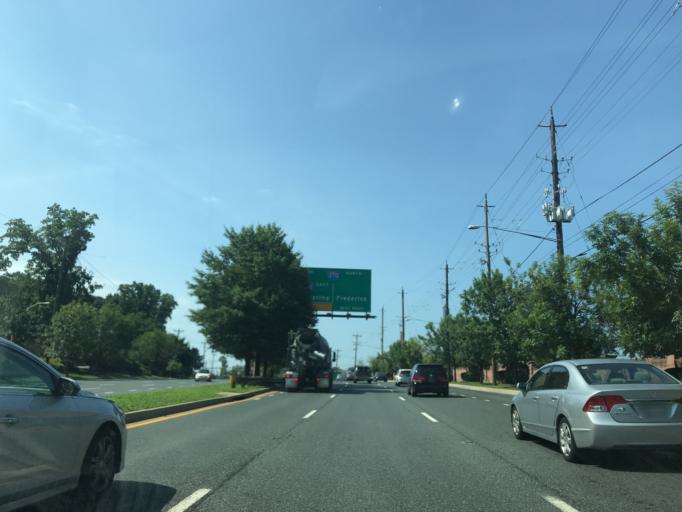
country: US
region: Maryland
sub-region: Montgomery County
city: North Bethesda
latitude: 39.0334
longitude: -77.1256
